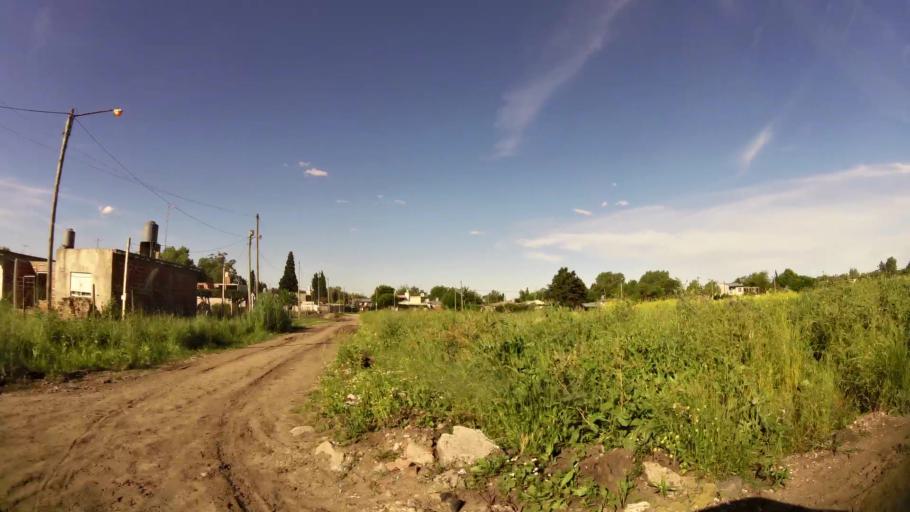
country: AR
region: Buenos Aires
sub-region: Partido de Almirante Brown
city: Adrogue
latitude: -34.8249
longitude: -58.3568
